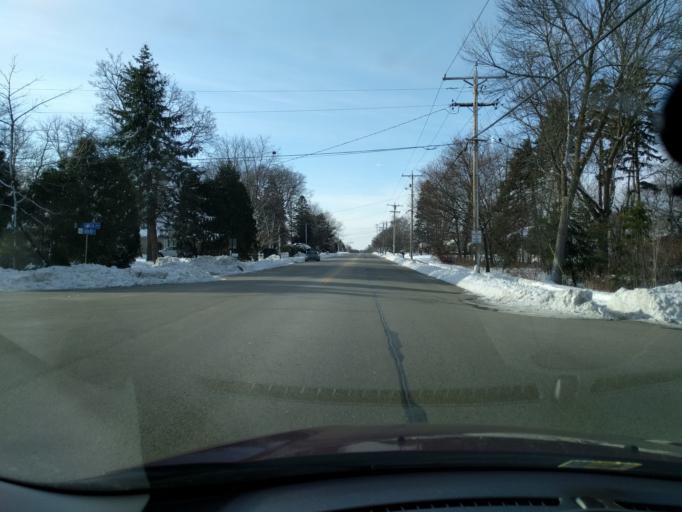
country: US
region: Wisconsin
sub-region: Milwaukee County
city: Fox Point
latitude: 43.1441
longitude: -87.9091
